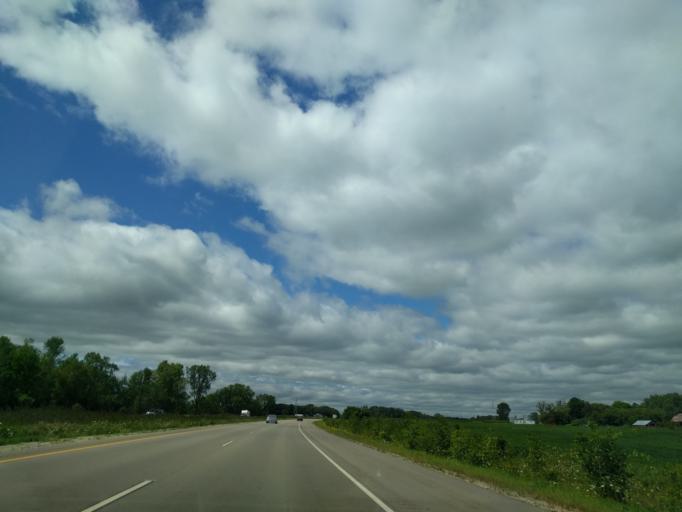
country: US
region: Wisconsin
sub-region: Oconto County
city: Oconto
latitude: 44.8014
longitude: -87.9875
